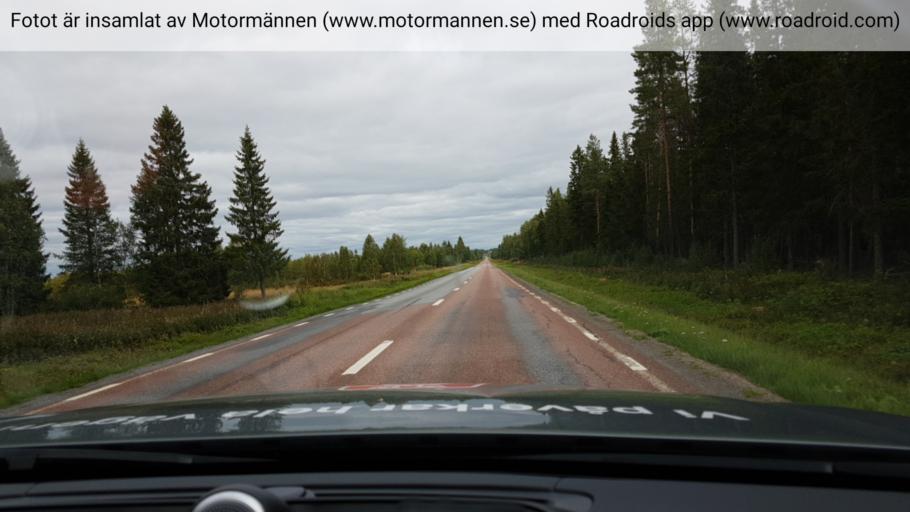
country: SE
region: Jaemtland
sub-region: Stroemsunds Kommun
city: Stroemsund
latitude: 63.7875
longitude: 15.5115
